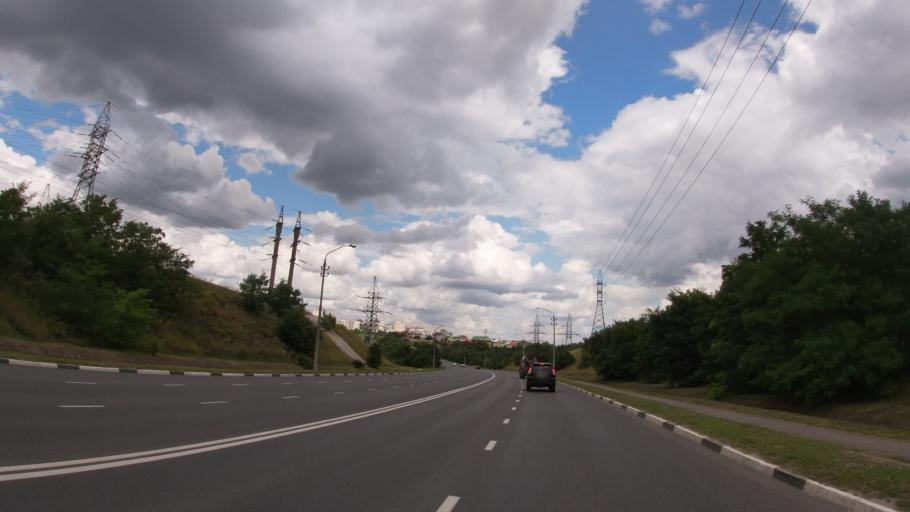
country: RU
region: Belgorod
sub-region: Belgorodskiy Rayon
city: Belgorod
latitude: 50.5566
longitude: 36.5852
